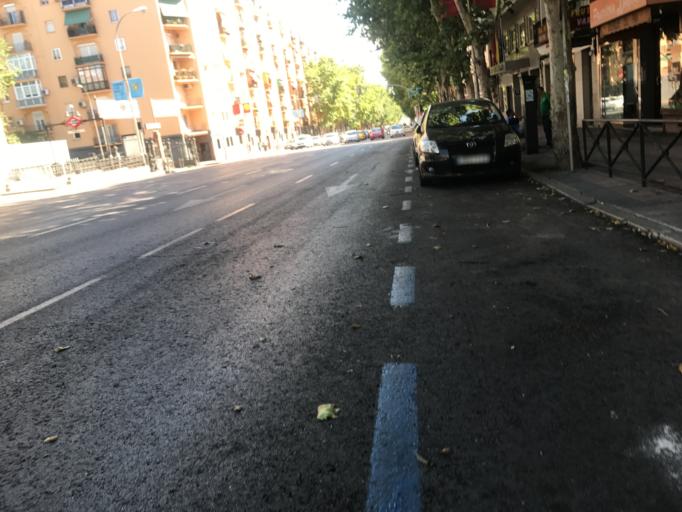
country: ES
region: Madrid
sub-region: Provincia de Madrid
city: Arganzuela
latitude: 40.4006
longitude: -3.6940
